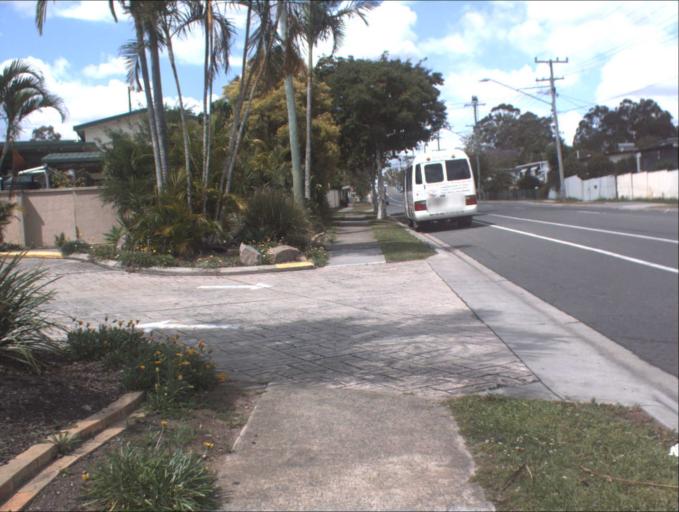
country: AU
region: Queensland
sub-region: Logan
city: Woodridge
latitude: -27.6198
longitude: 153.1004
